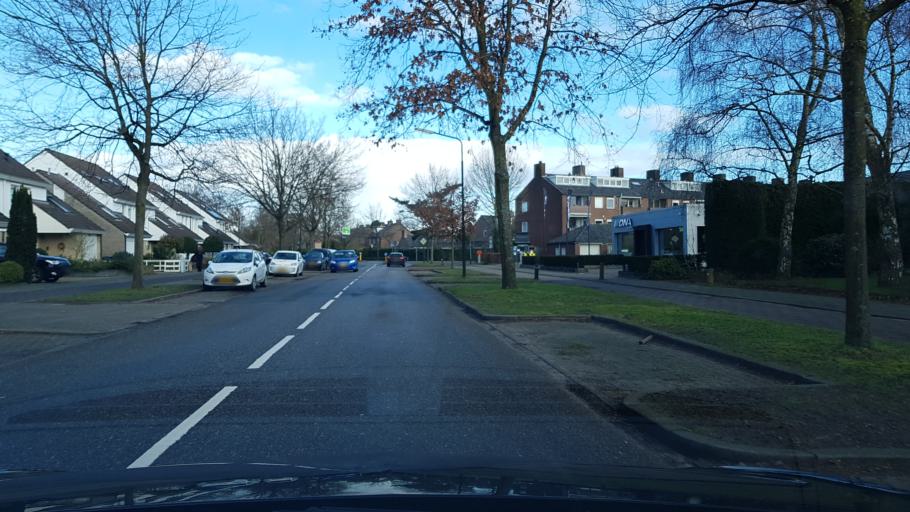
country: NL
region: North Holland
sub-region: Gemeente Bussum
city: Bussum
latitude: 52.2838
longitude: 5.1478
